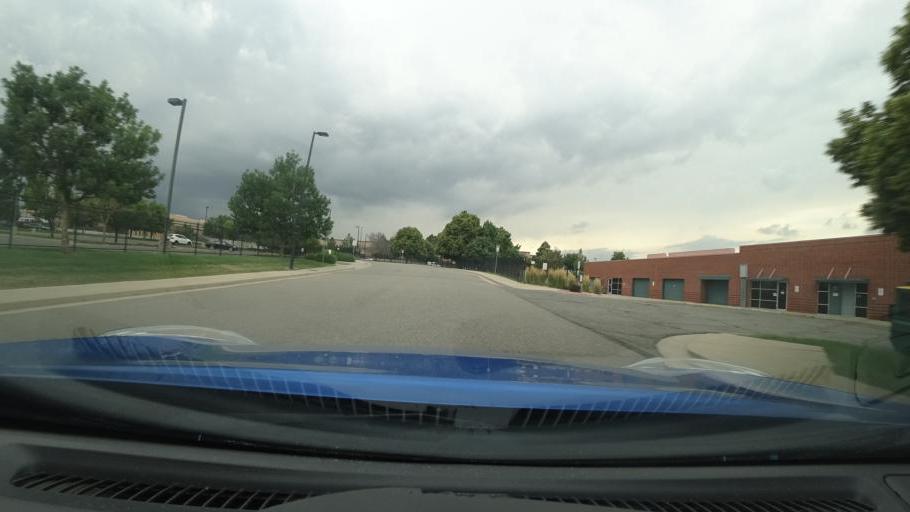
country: US
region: Colorado
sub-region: Adams County
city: Aurora
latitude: 39.7021
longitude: -104.8236
